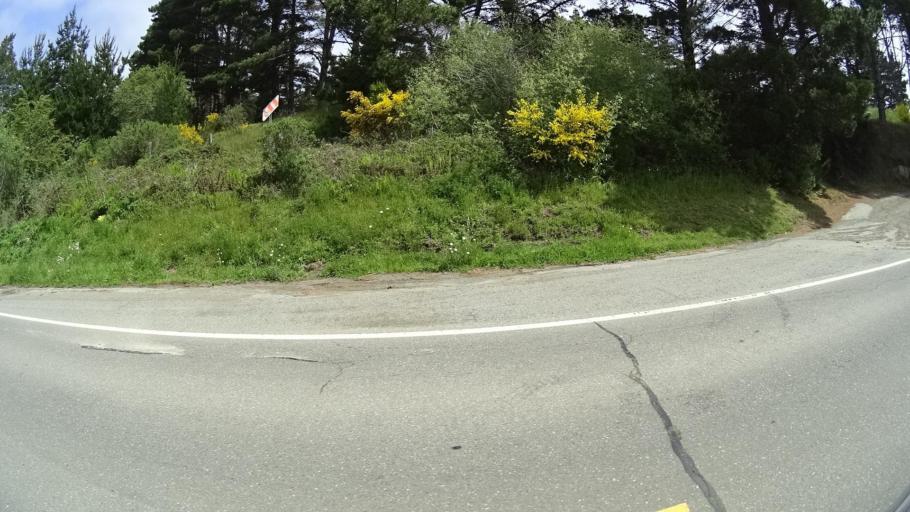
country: US
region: California
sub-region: Humboldt County
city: Humboldt Hill
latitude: 40.6945
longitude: -124.1978
